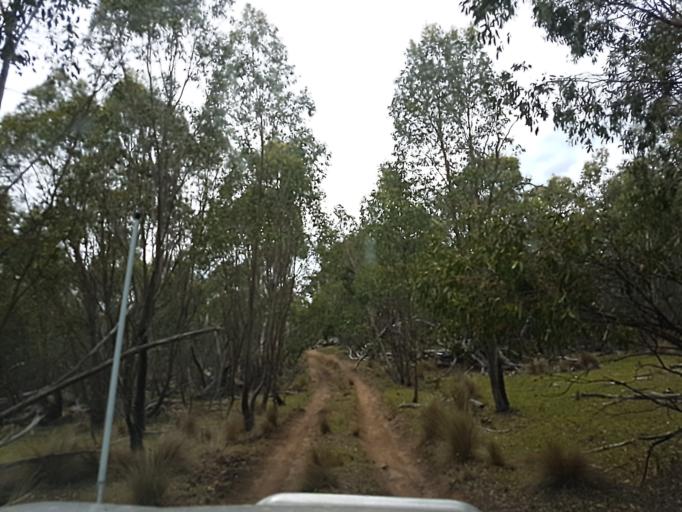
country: AU
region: New South Wales
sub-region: Snowy River
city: Jindabyne
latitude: -36.8553
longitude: 148.2624
